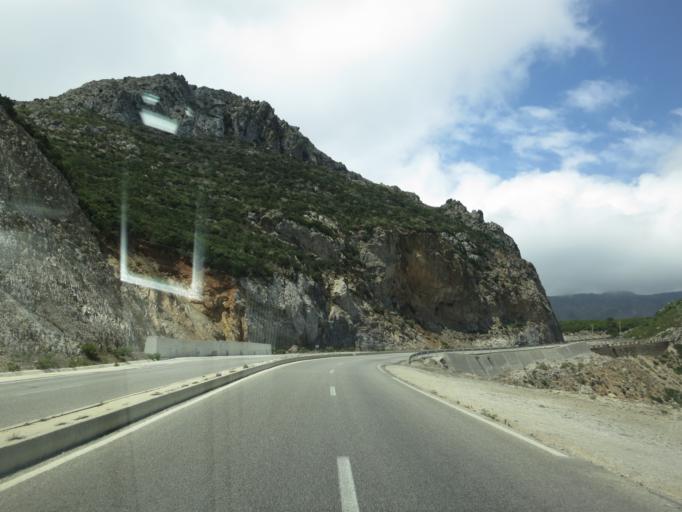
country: ES
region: Ceuta
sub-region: Ceuta
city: Ceuta
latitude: 35.8732
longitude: -5.3907
